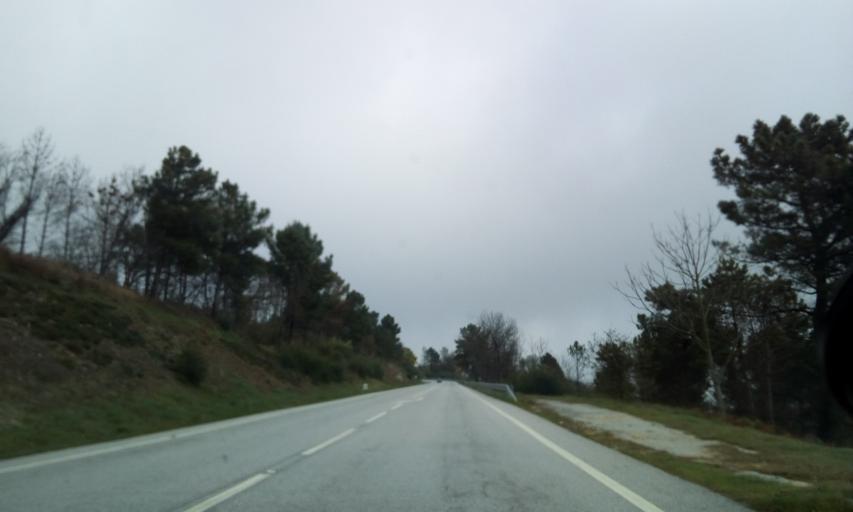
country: PT
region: Guarda
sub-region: Fornos de Algodres
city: Fornos de Algodres
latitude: 40.6879
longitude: -7.4691
